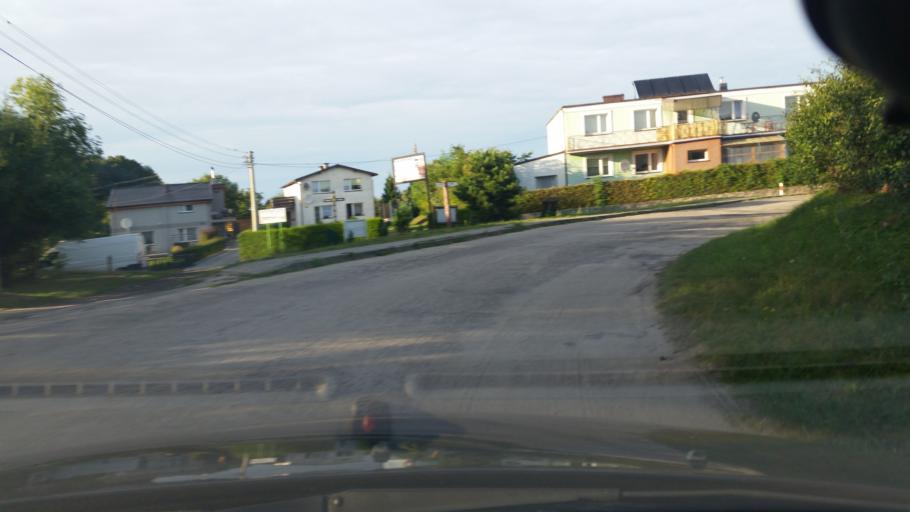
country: PL
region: Pomeranian Voivodeship
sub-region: Powiat wejherowski
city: Choczewo
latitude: 54.7700
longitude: 17.7942
